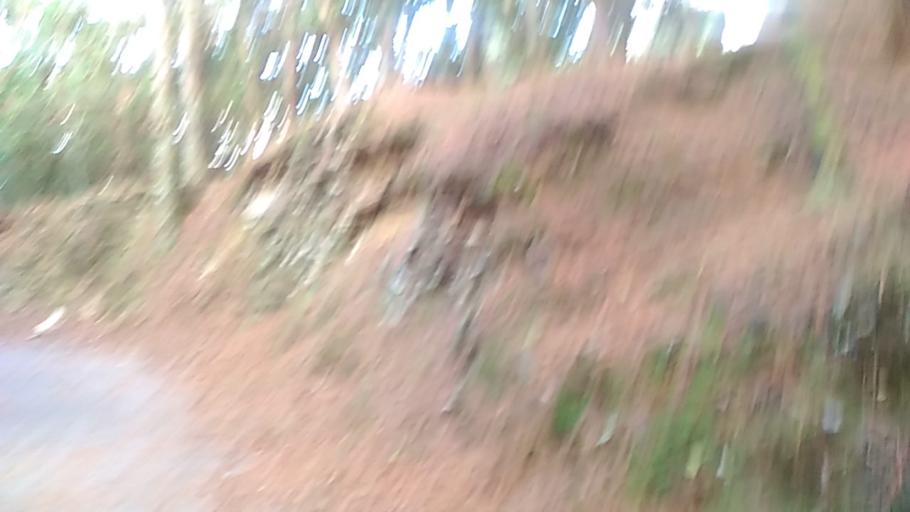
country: TW
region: Taiwan
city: Daxi
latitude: 24.4084
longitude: 121.3043
